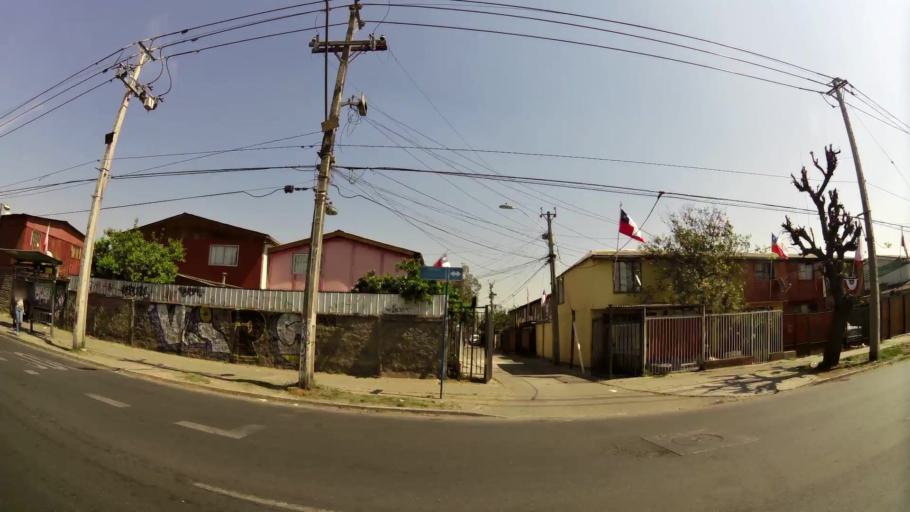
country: CL
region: Santiago Metropolitan
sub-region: Provincia de Santiago
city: La Pintana
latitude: -33.5537
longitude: -70.6129
